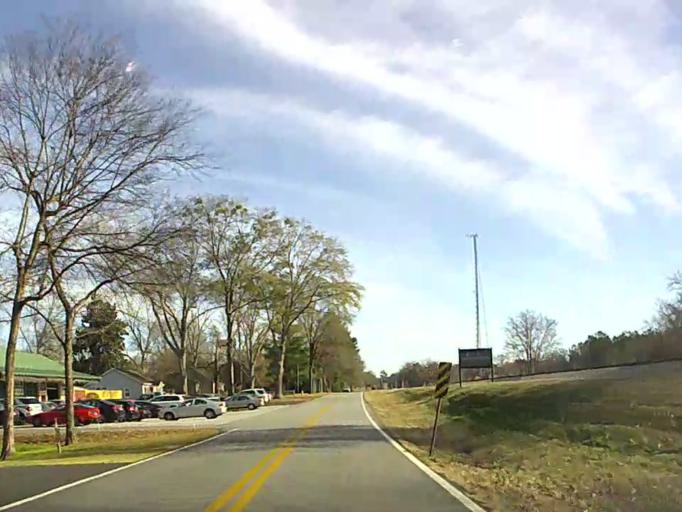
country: US
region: Georgia
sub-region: Bibb County
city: West Point
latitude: 32.9486
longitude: -83.8011
